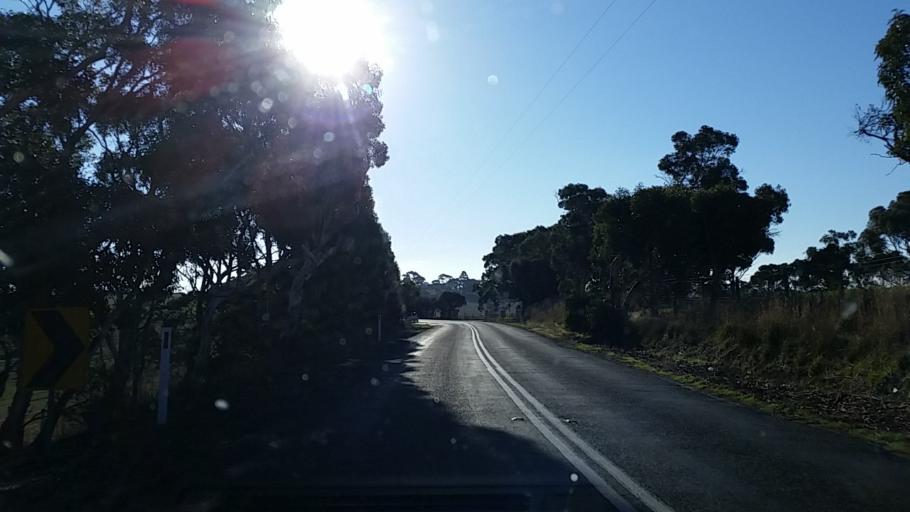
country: AU
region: South Australia
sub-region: Mount Barker
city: Mount Barker
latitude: -35.1273
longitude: 138.9063
